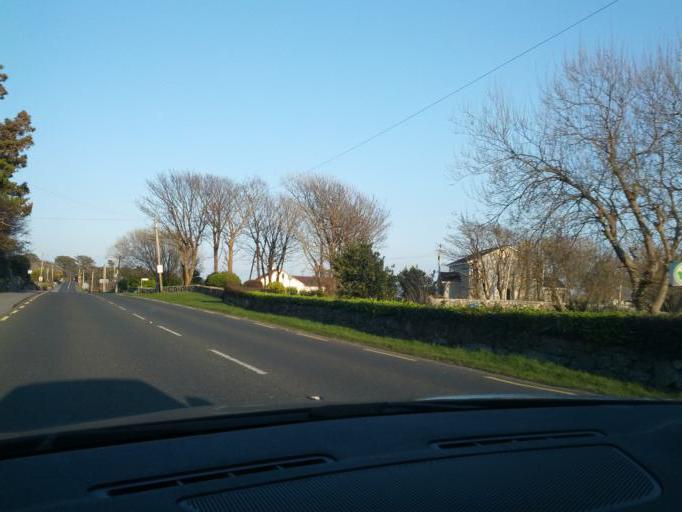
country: IE
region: Connaught
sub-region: County Galway
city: Moycullen
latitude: 53.2441
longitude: -9.3197
